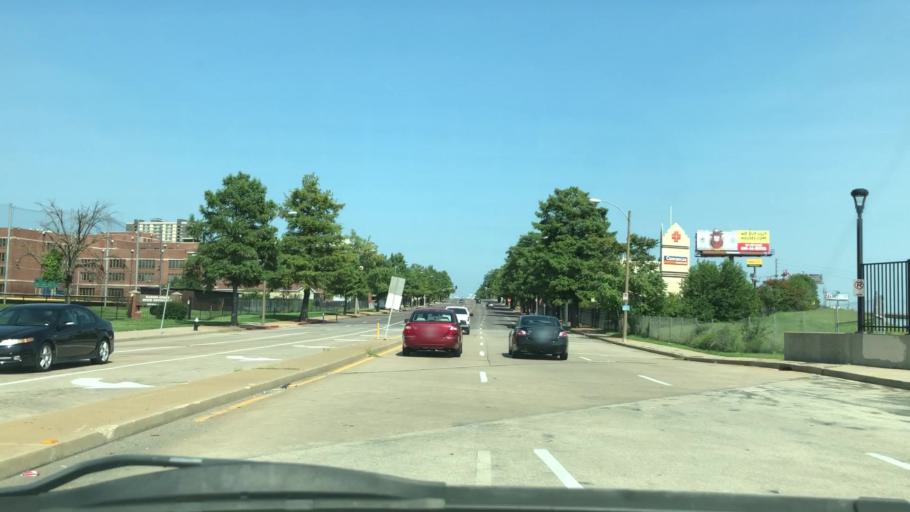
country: US
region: Missouri
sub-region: City of Saint Louis
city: St. Louis
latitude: 38.6310
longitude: -90.2270
